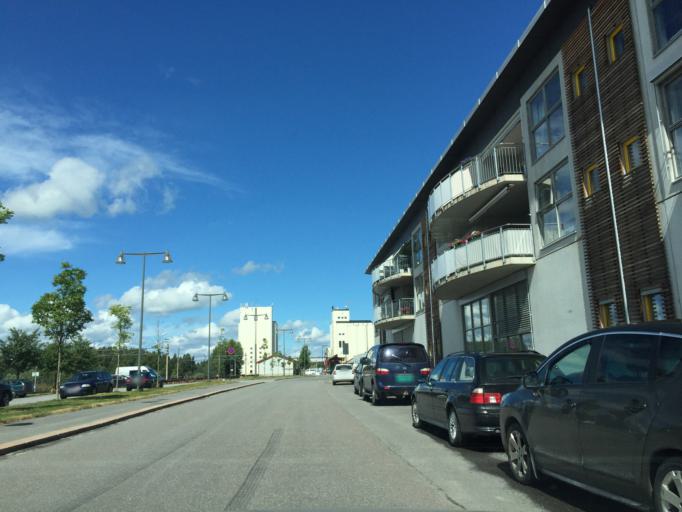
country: NO
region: Akershus
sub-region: Nes
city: Arnes
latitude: 60.1243
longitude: 11.4662
